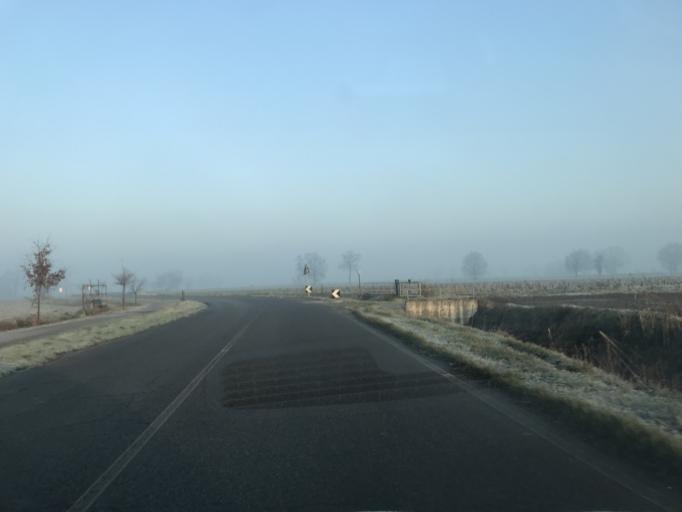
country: IT
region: Lombardy
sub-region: Provincia di Lodi
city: Bargano
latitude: 45.2451
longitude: 9.4414
